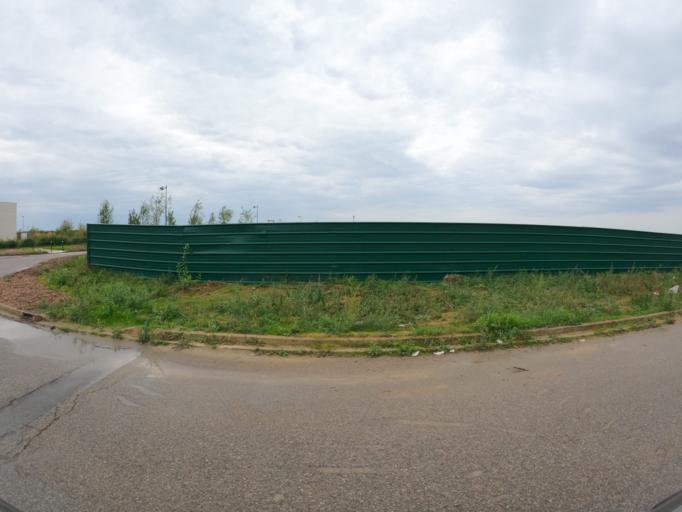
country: FR
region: Ile-de-France
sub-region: Departement de Seine-et-Marne
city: Serris
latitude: 48.8373
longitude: 2.8011
